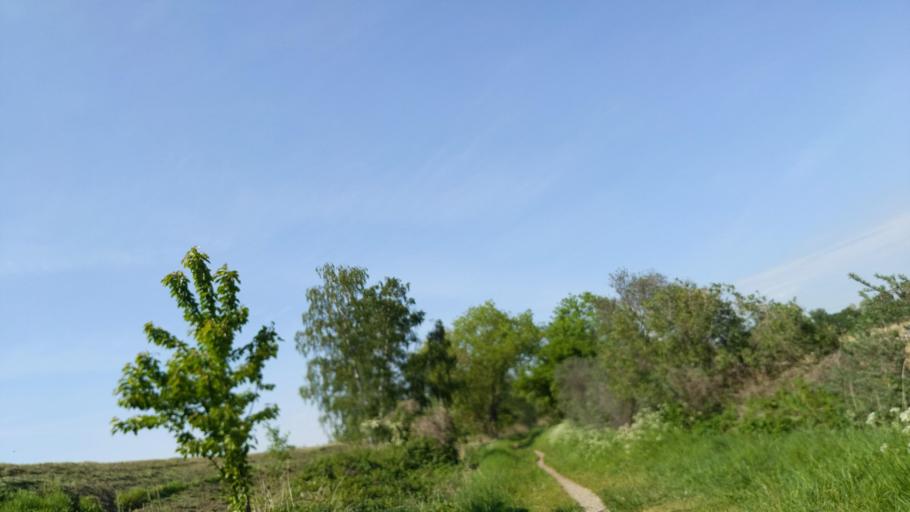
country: DE
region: Schleswig-Holstein
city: Ratekau
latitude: 53.8930
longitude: 10.7666
